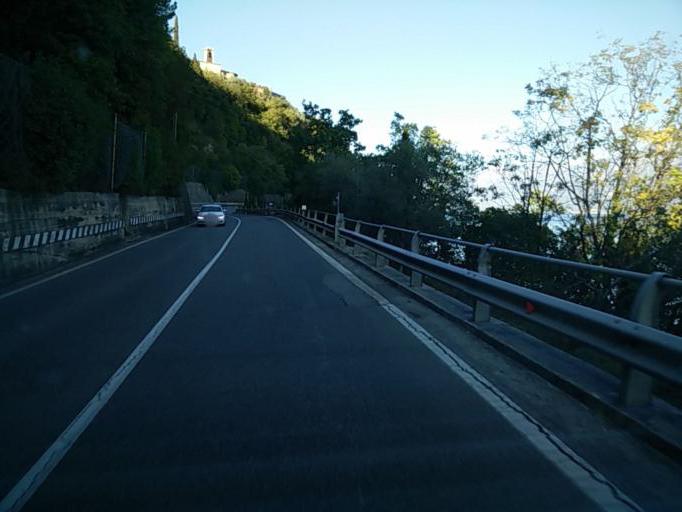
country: IT
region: Lombardy
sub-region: Provincia di Brescia
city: Gargnano
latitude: 45.6636
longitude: 10.6450
